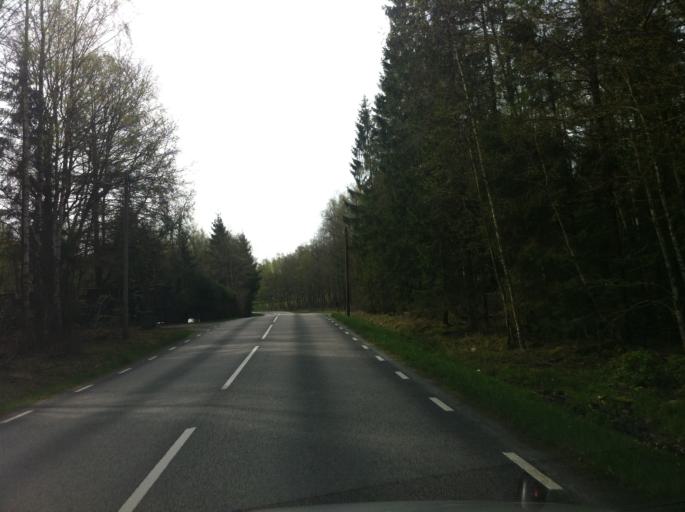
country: SE
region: Vaestra Goetaland
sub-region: Marks Kommun
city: Kinna
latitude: 57.4585
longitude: 12.7210
